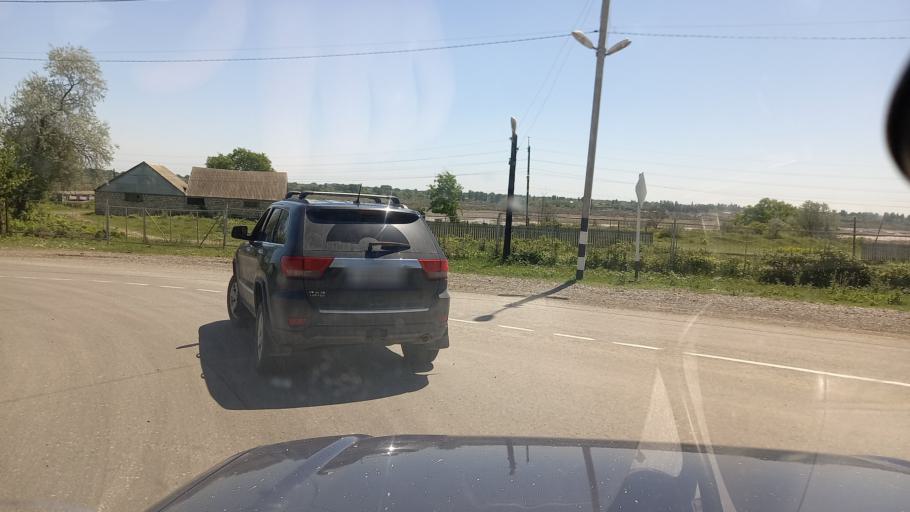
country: RU
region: Dagestan
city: Novaya Maka
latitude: 41.7363
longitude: 48.4415
